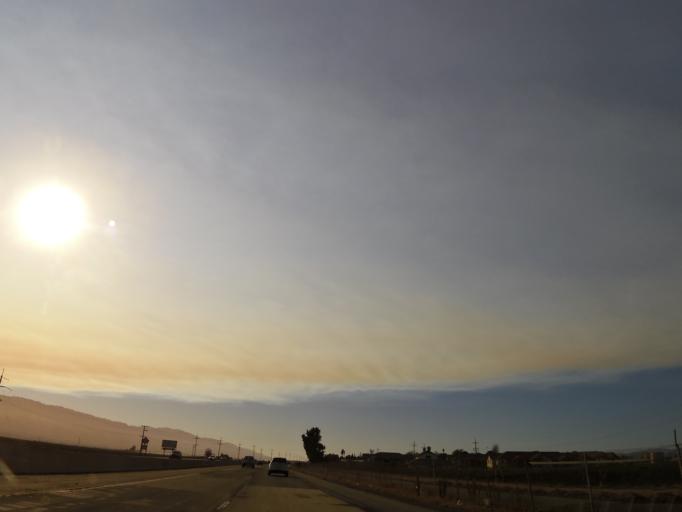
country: US
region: California
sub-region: Monterey County
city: Soledad
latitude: 36.4565
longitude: -121.3745
